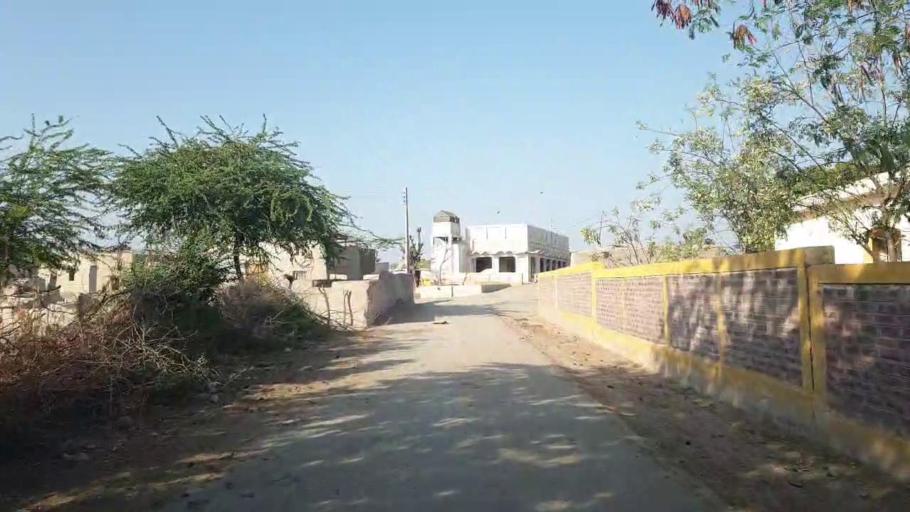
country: PK
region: Sindh
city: Chor
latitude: 25.5416
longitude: 69.7316
